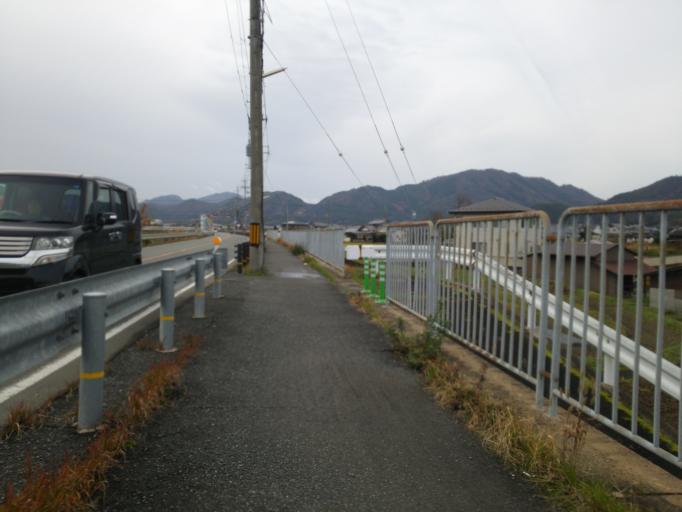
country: JP
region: Kyoto
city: Kameoka
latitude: 35.0055
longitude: 135.5572
